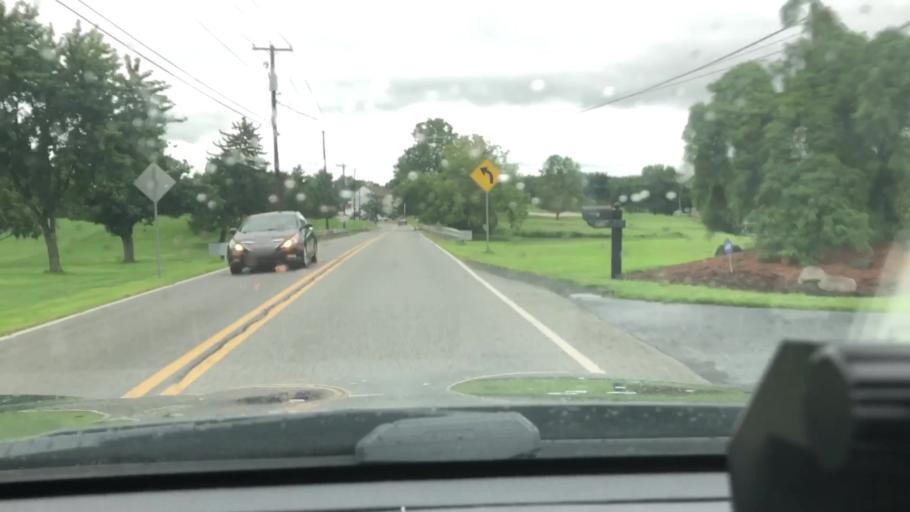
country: US
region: Pennsylvania
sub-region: Montgomery County
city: Halfway House
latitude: 40.2957
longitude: -75.6238
